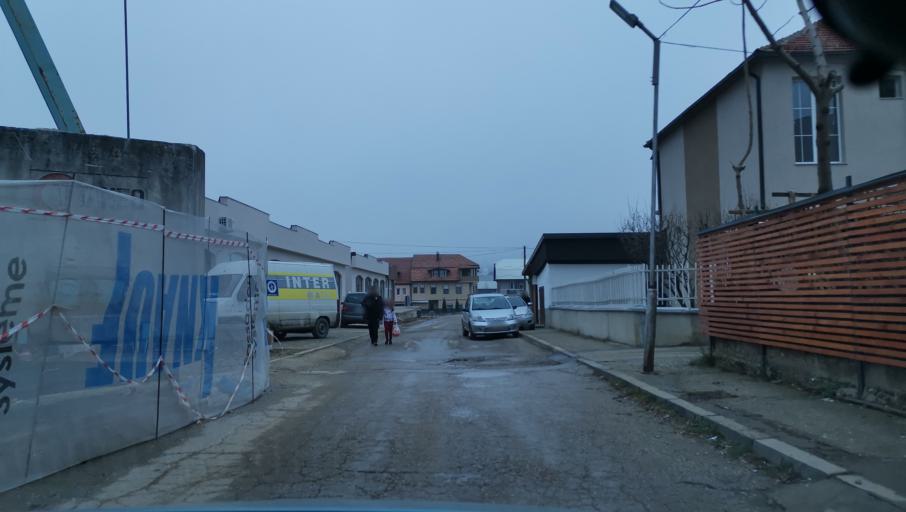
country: MK
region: Debar
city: Debar
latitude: 41.5177
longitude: 20.5273
